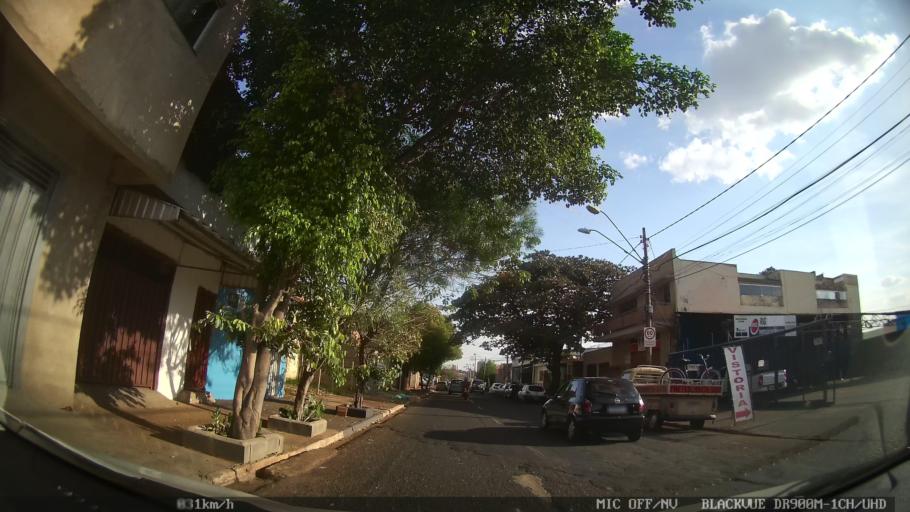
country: BR
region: Sao Paulo
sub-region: Ribeirao Preto
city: Ribeirao Preto
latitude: -21.1608
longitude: -47.8096
